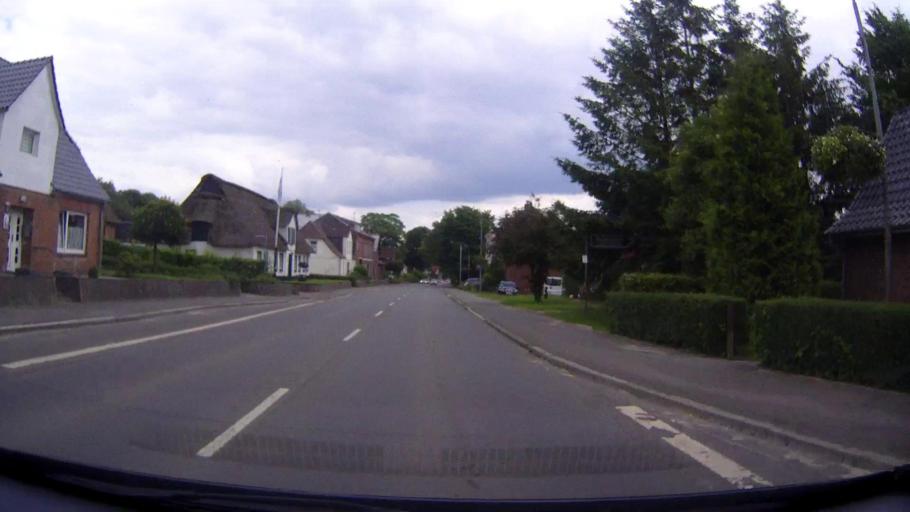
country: DE
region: Schleswig-Holstein
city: Hanerau-Hademarschen
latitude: 54.1209
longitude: 9.4371
